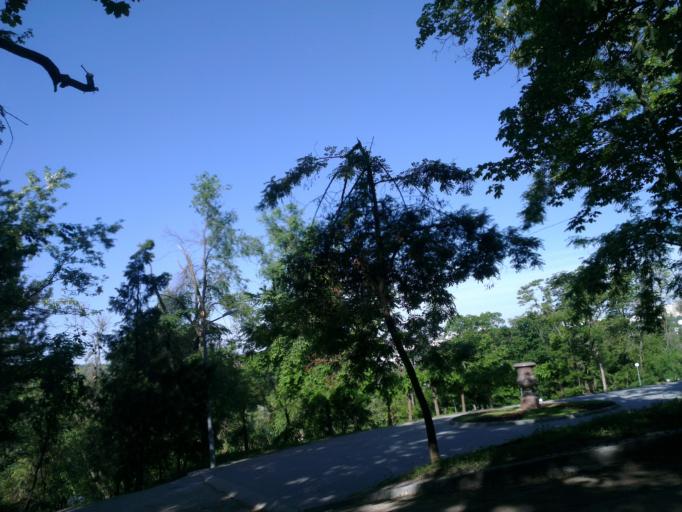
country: MD
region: Chisinau
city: Chisinau
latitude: 47.0219
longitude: 28.8171
